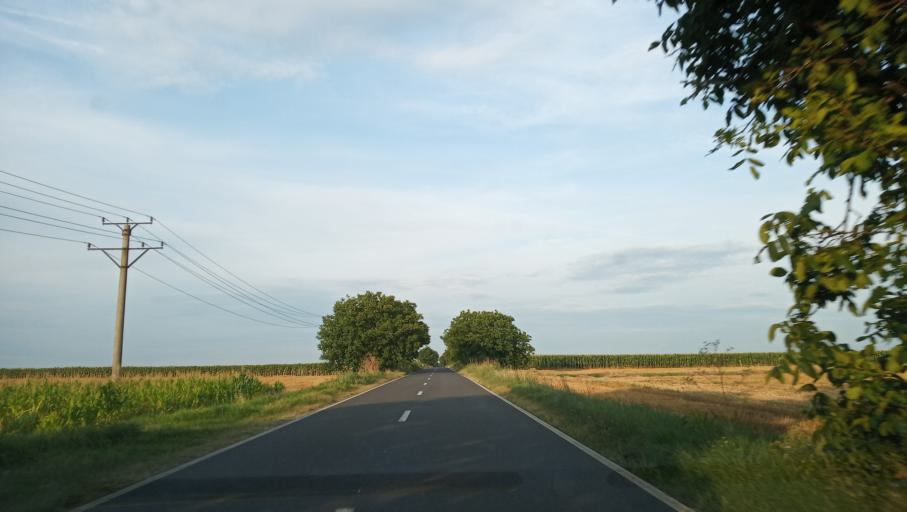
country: RO
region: Giurgiu
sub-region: Comuna Prundu
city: Prundu
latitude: 44.1021
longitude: 26.2812
